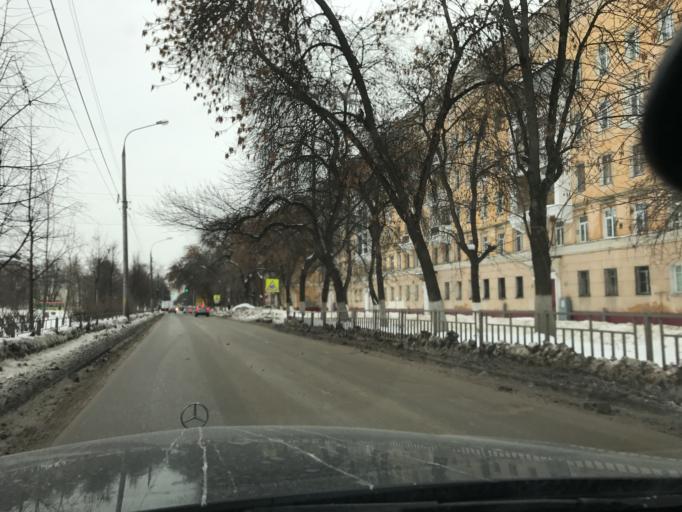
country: RU
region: Nizjnij Novgorod
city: Gorbatovka
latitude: 56.2464
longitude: 43.8475
